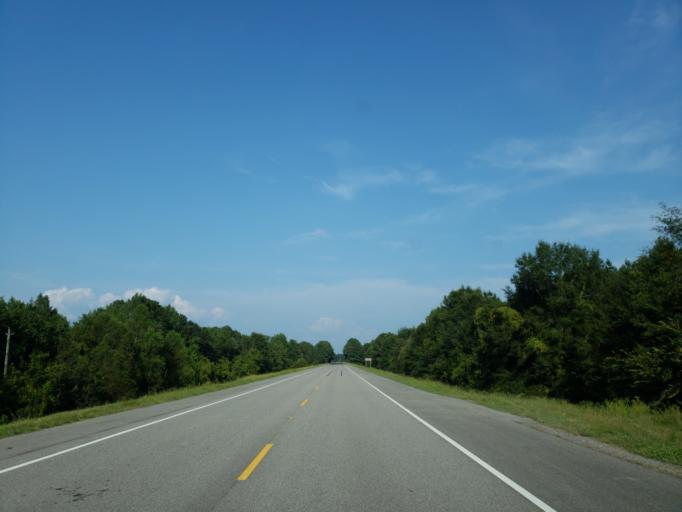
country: US
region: Alabama
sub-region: Sumter County
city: Livingston
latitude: 32.6974
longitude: -88.1072
